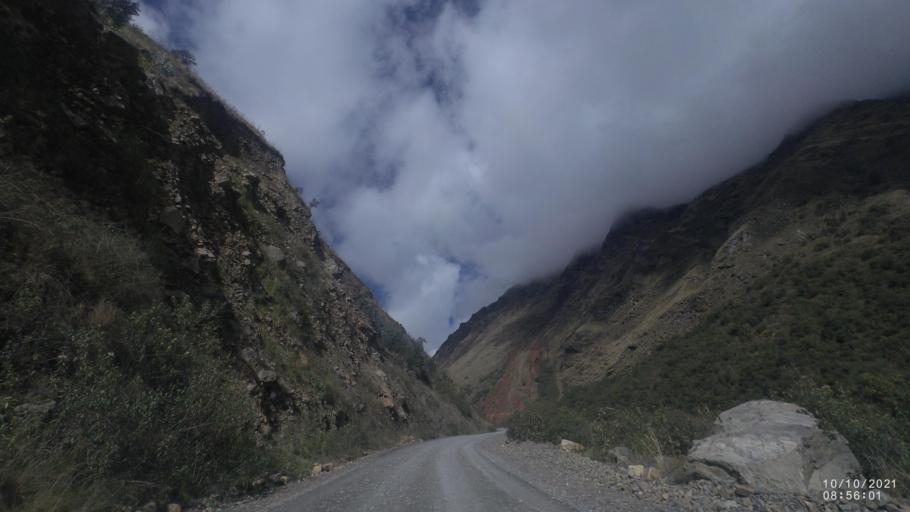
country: BO
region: La Paz
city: Quime
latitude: -16.9882
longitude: -67.2421
